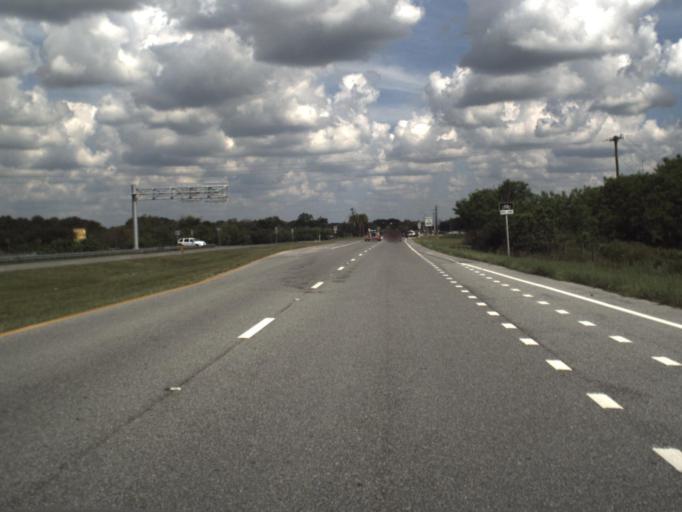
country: US
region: Florida
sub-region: Sarasota County
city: Fruitville
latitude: 27.3384
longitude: -82.4417
